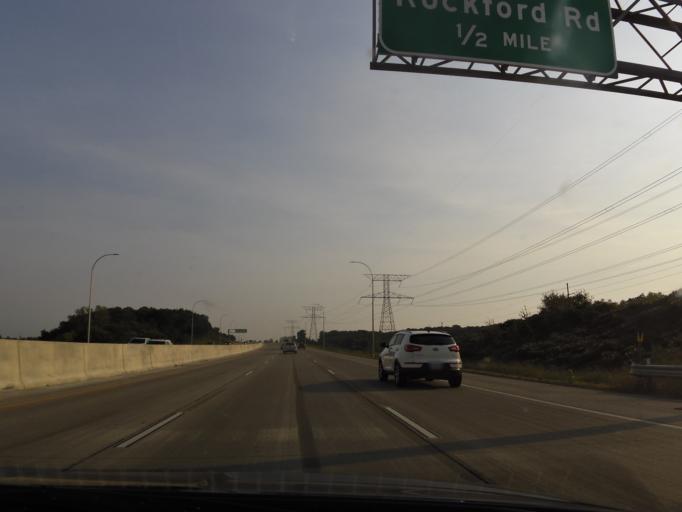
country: US
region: Minnesota
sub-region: Hennepin County
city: Plymouth
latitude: 45.0404
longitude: -93.4530
